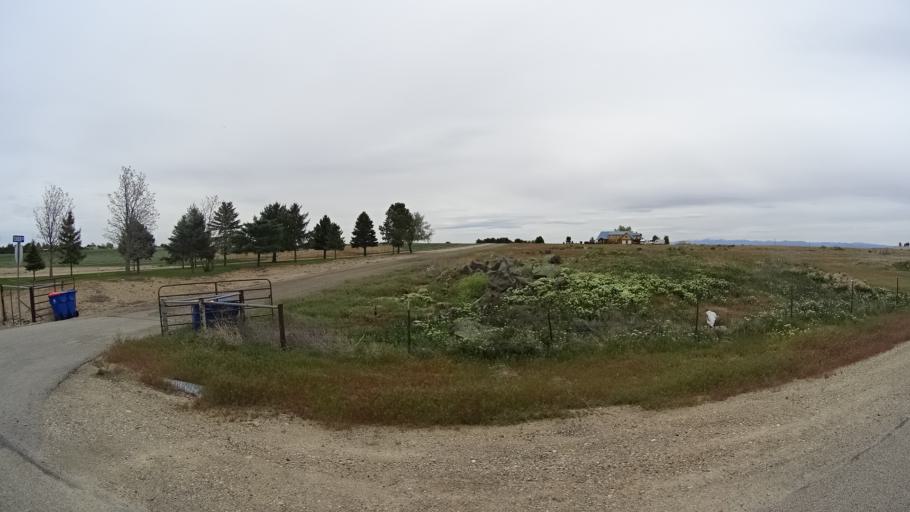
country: US
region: Idaho
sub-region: Ada County
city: Kuna
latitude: 43.4877
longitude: -116.3443
